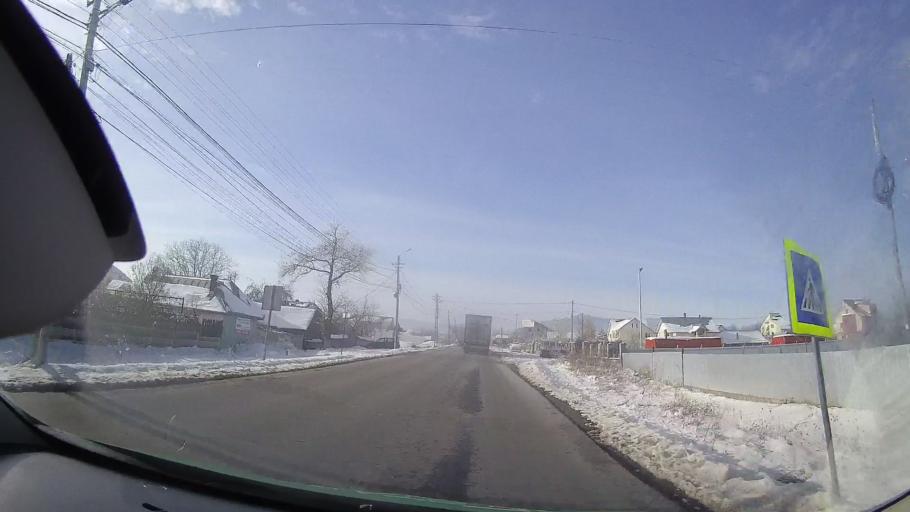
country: RO
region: Neamt
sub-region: Oras Targu Neamt
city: Targu Neamt
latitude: 47.2090
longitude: 26.3984
